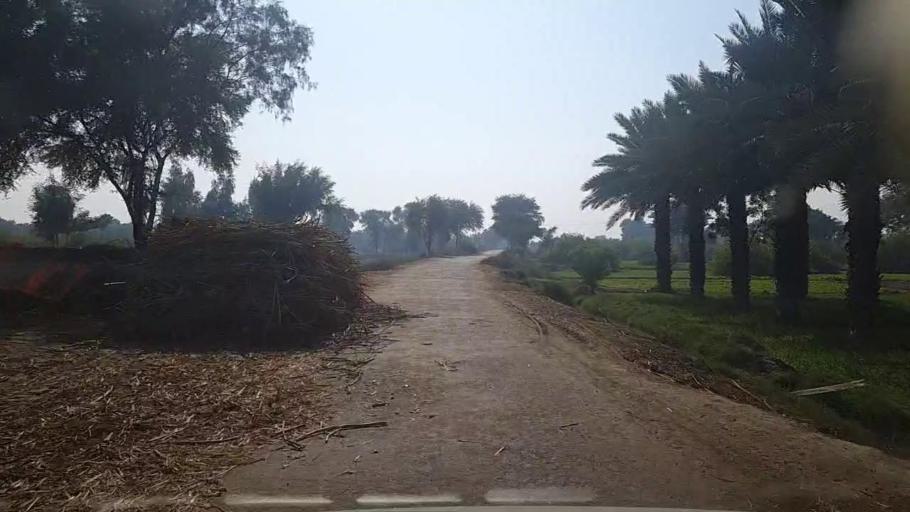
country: PK
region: Sindh
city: Kandiari
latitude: 26.9898
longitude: 68.4695
